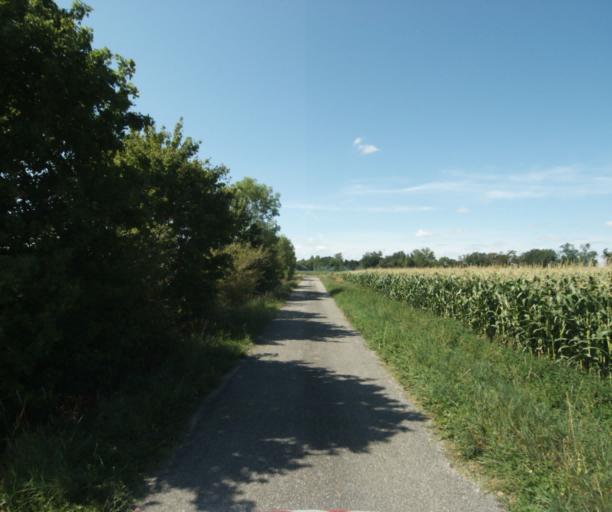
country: FR
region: Midi-Pyrenees
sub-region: Departement de la Haute-Garonne
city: Revel
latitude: 43.4871
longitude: 1.9735
